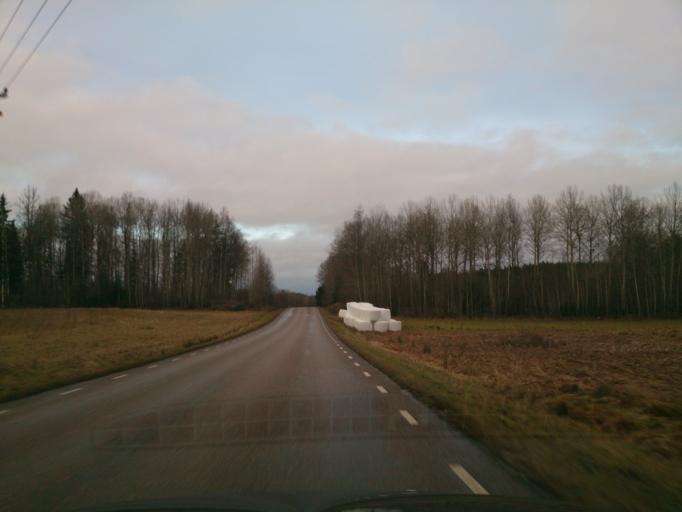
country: SE
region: OEstergoetland
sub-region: Atvidabergs Kommun
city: Atvidaberg
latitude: 58.2754
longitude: 16.0323
